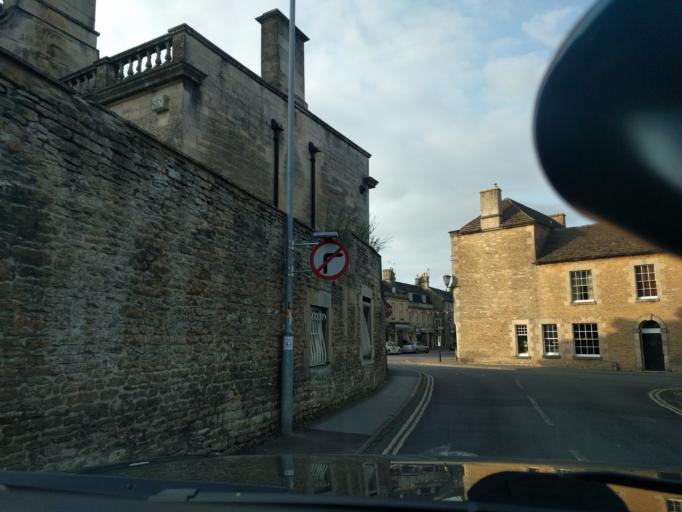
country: GB
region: England
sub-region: Wiltshire
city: Corsham
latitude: 51.4308
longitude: -2.1858
